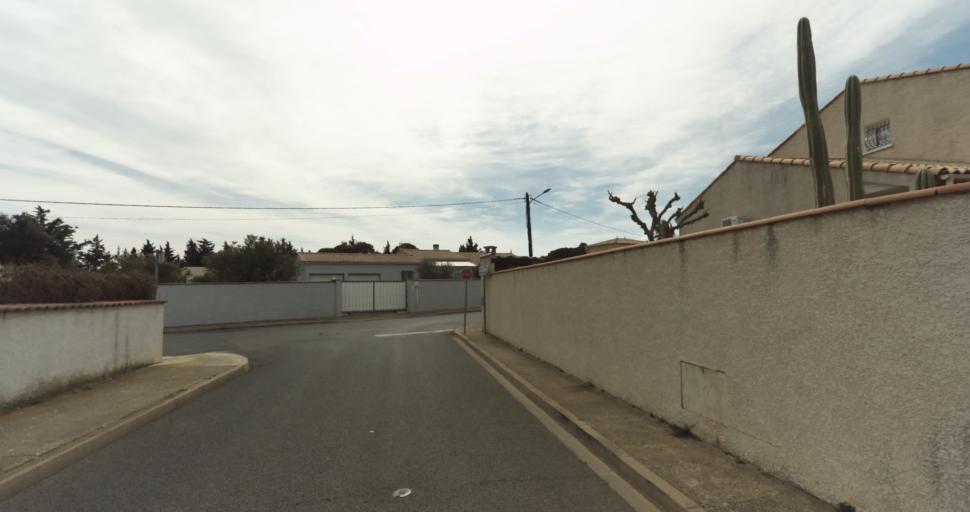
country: FR
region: Languedoc-Roussillon
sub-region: Departement de l'Herault
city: Marseillan
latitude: 43.3351
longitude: 3.5281
